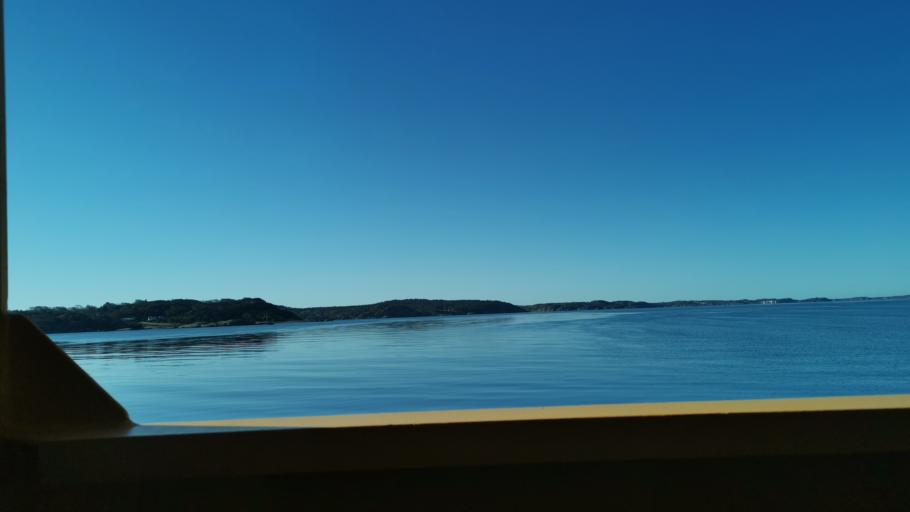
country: SE
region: Vaestra Goetaland
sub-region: Lysekils Kommun
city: Brastad
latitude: 58.3029
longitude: 11.5256
